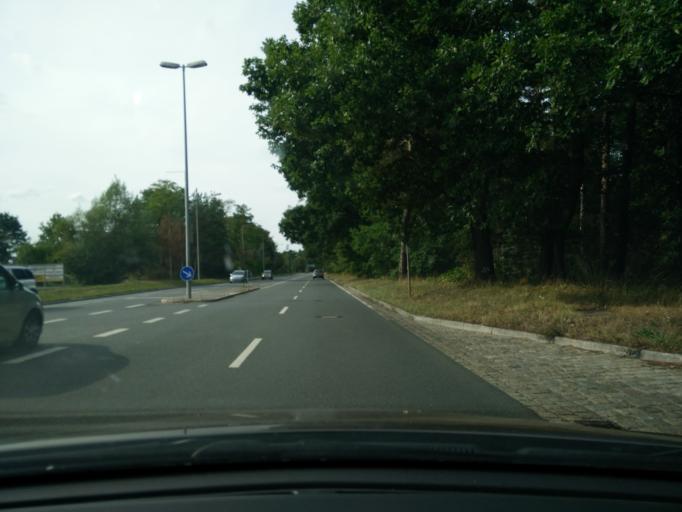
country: DE
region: Bavaria
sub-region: Regierungsbezirk Mittelfranken
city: Wendelstein
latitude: 49.4176
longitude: 11.1362
